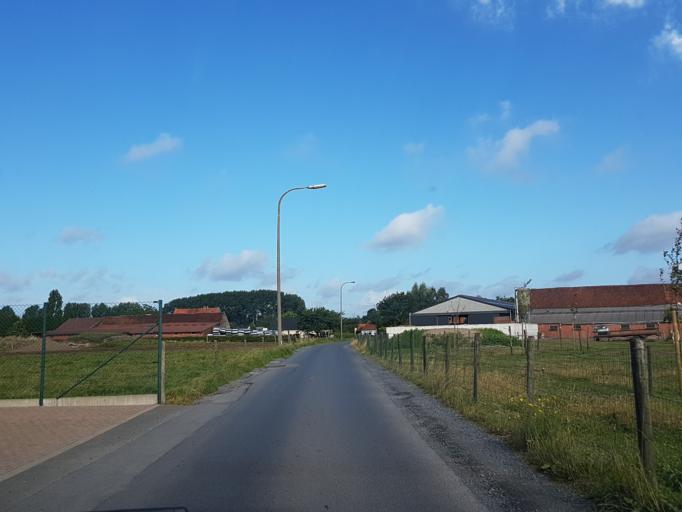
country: BE
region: Flanders
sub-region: Provincie Oost-Vlaanderen
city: Nevele
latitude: 51.0627
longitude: 3.5627
